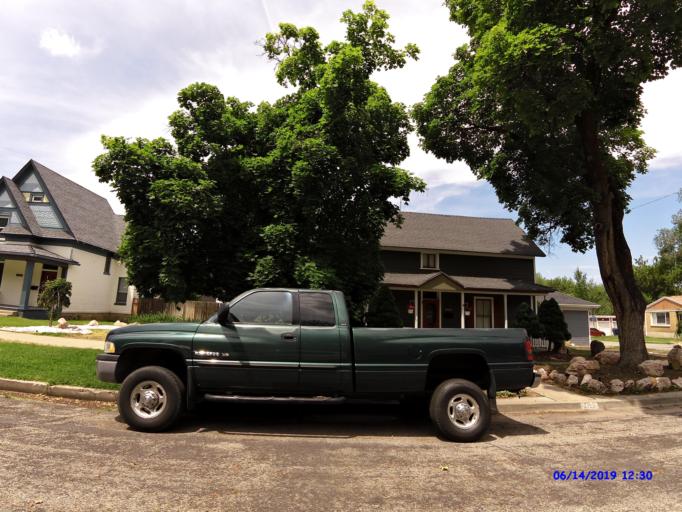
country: US
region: Utah
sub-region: Weber County
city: Ogden
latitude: 41.2213
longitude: -111.9511
